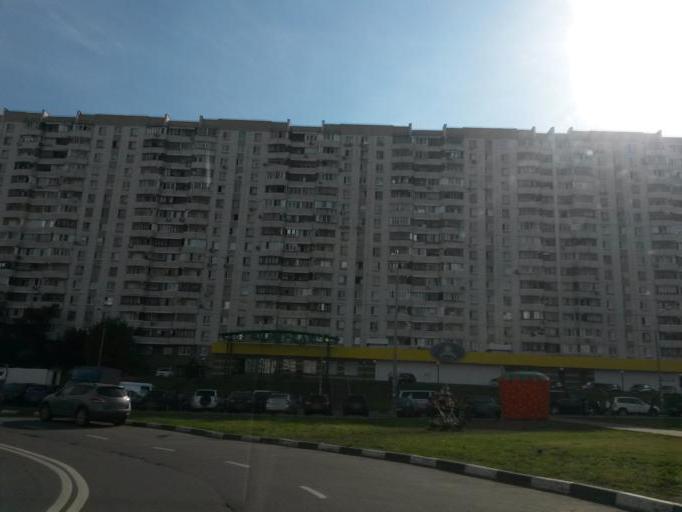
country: RU
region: Moscow
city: Brateyevo
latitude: 55.6342
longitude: 37.7644
